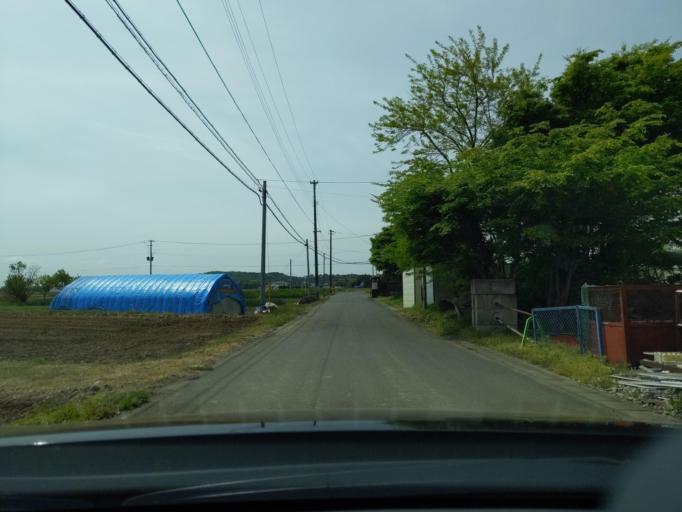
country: JP
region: Fukushima
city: Koriyama
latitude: 37.4044
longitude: 140.2726
